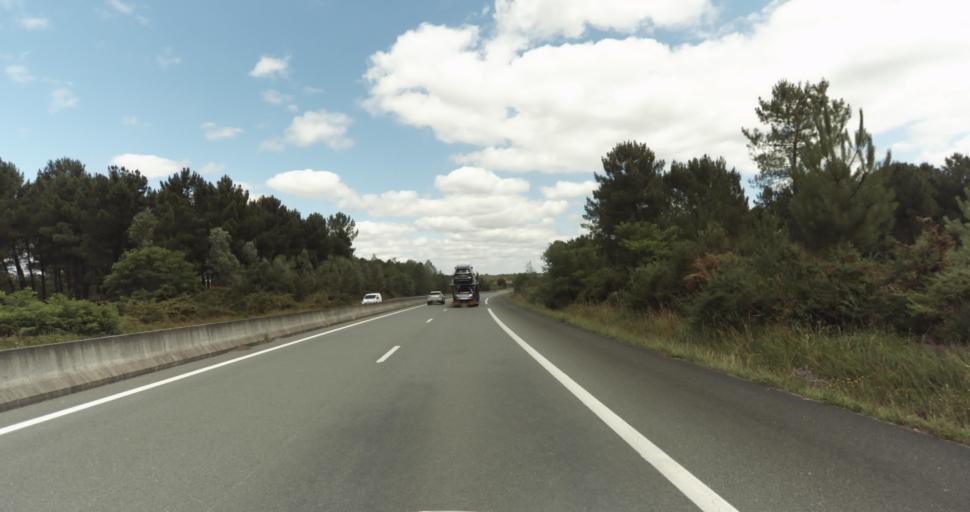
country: FR
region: Aquitaine
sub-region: Departement de la Gironde
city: Saint-Macaire
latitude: 44.5150
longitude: -0.1999
